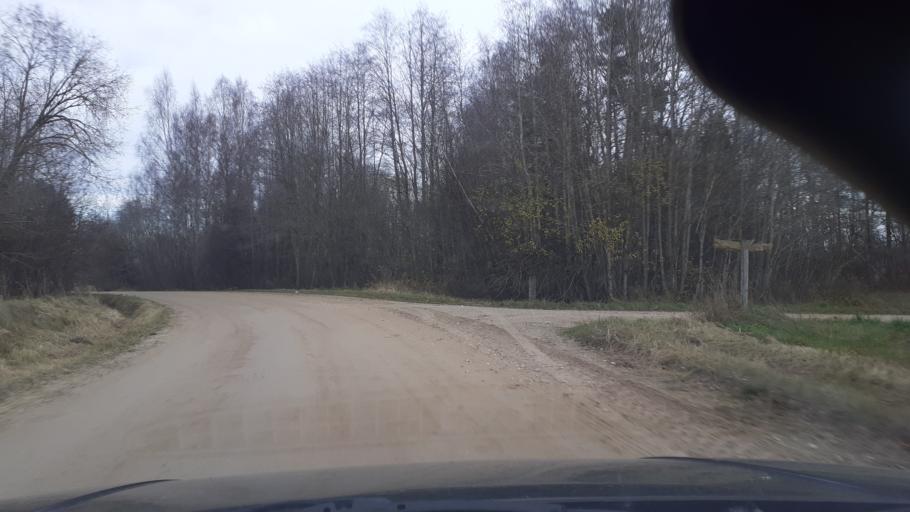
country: LV
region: Alsunga
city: Alsunga
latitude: 56.9995
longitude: 21.6760
